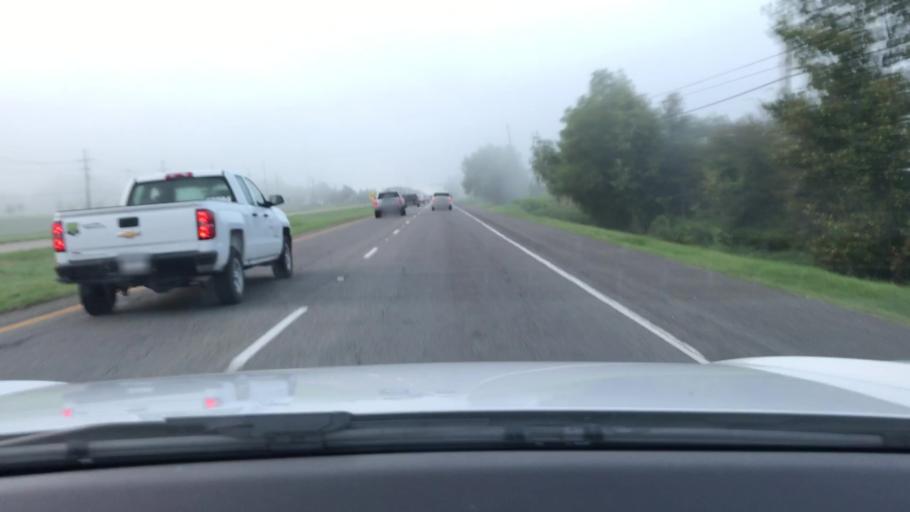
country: US
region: Louisiana
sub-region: West Baton Rouge Parish
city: Addis
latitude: 30.3364
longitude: -91.2589
